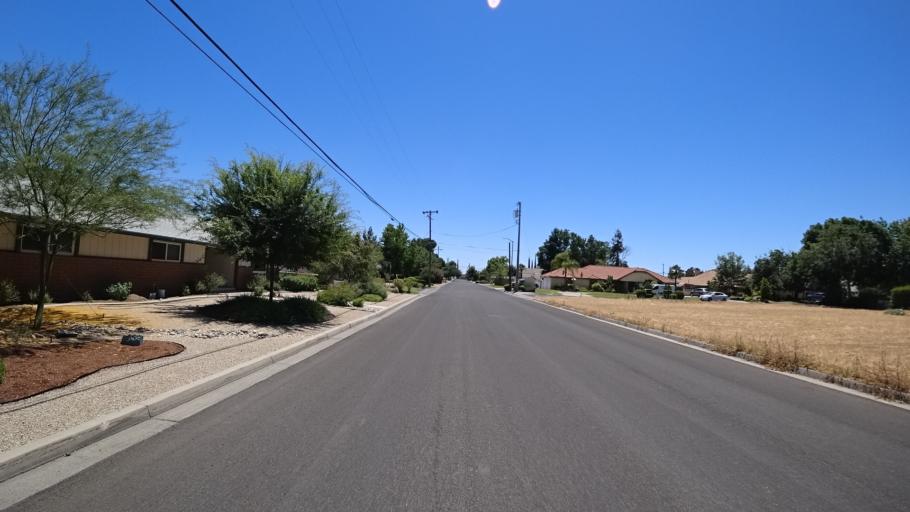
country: US
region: California
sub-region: Fresno County
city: Tarpey Village
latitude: 36.8045
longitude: -119.7520
